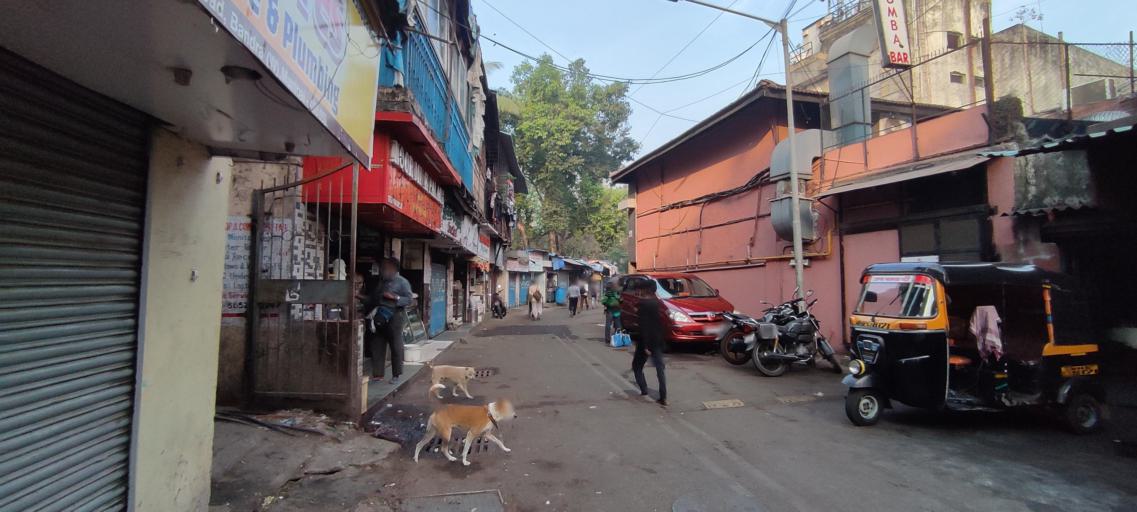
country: IN
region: Maharashtra
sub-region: Mumbai Suburban
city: Mumbai
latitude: 19.0550
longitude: 72.8392
